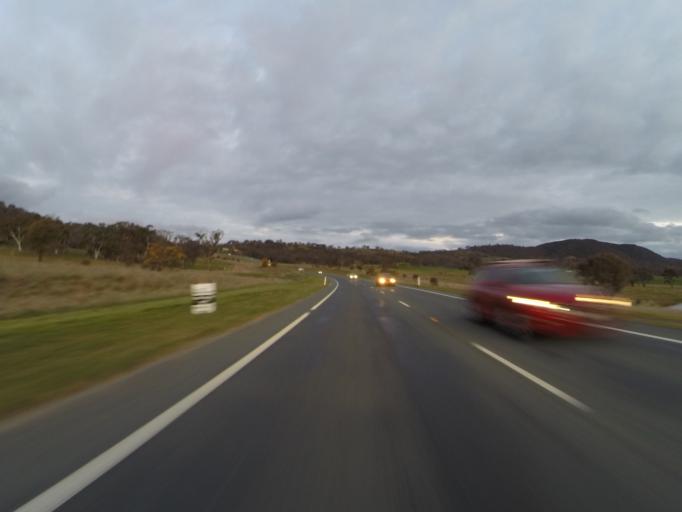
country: AU
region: Australian Capital Territory
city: Kaleen
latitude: -35.2103
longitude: 149.1733
